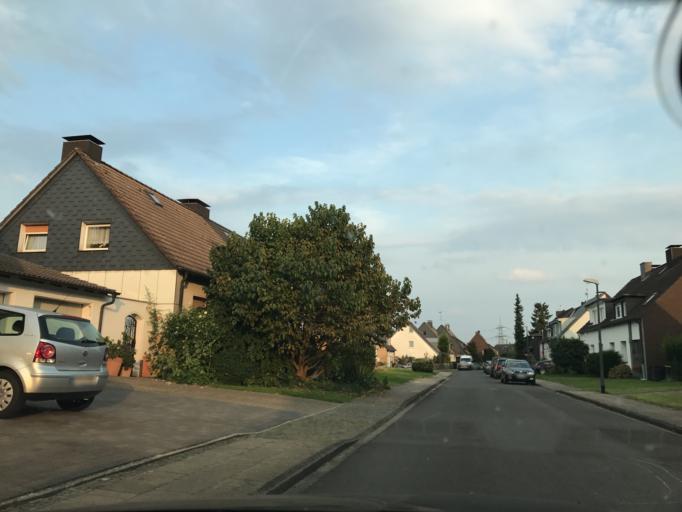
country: DE
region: North Rhine-Westphalia
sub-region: Regierungsbezirk Dusseldorf
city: Muelheim (Ruhr)
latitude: 51.4532
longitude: 6.9370
